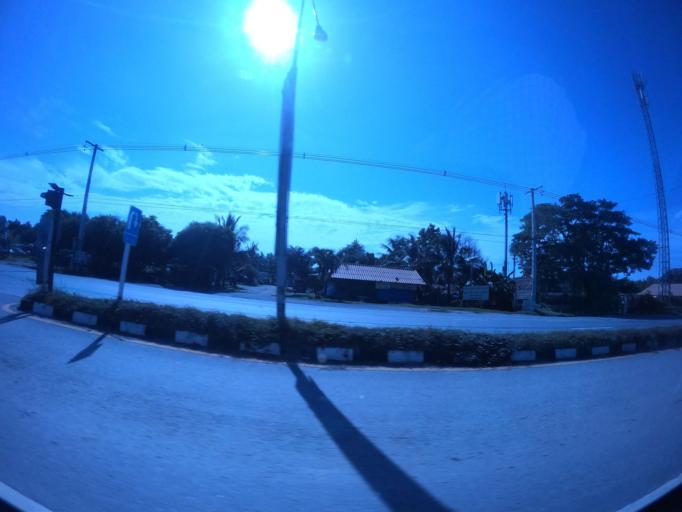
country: TH
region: Nakhon Nayok
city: Ban Na
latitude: 14.2363
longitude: 101.0709
